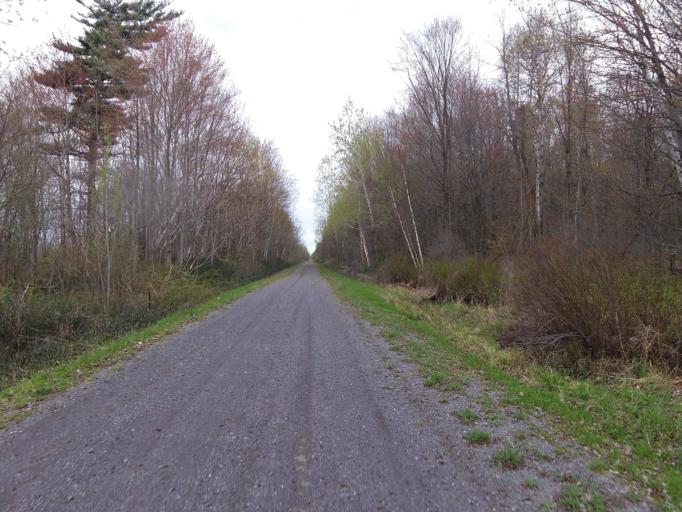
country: CA
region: Quebec
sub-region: Outaouais
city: Papineauville
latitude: 45.5167
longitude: -74.9418
